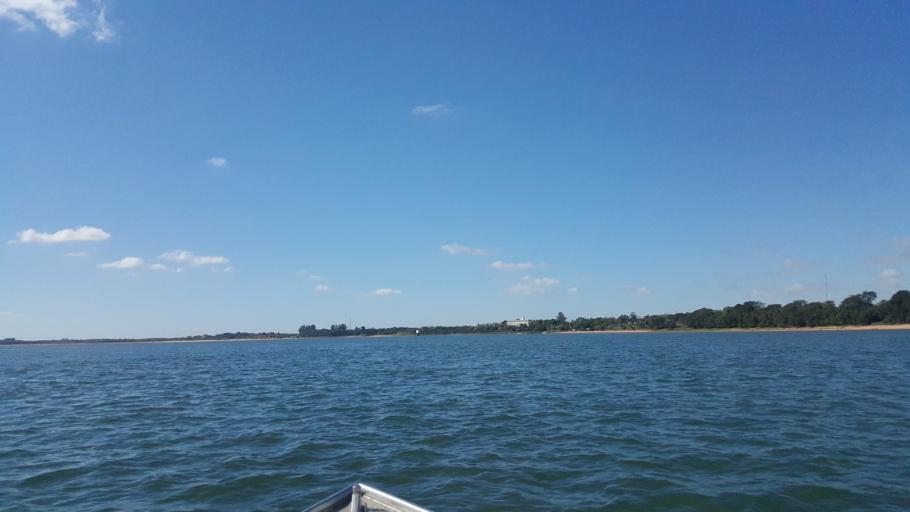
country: AR
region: Corrientes
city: Ituzaingo
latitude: -27.5807
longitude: -56.6934
